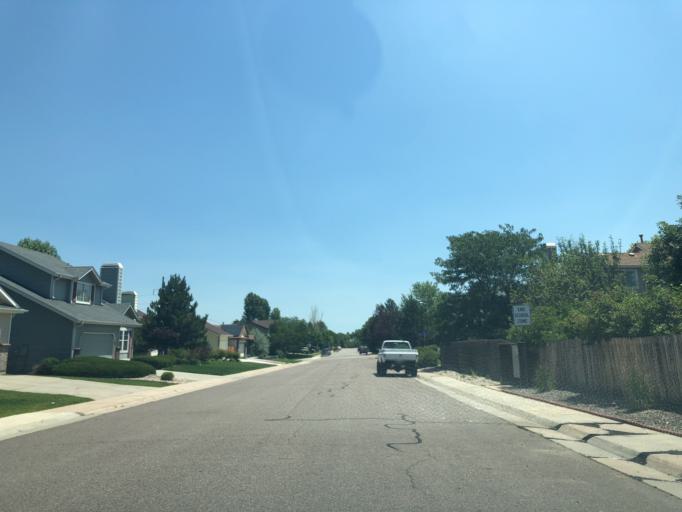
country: US
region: Colorado
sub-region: Arapahoe County
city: Dove Valley
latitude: 39.6236
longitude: -104.7606
